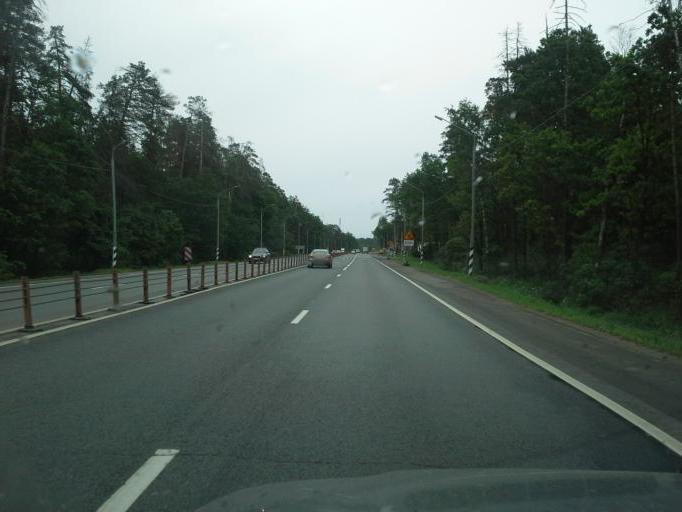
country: RU
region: Moskovskaya
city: Malaya Dubna
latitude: 55.8965
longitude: 39.0452
